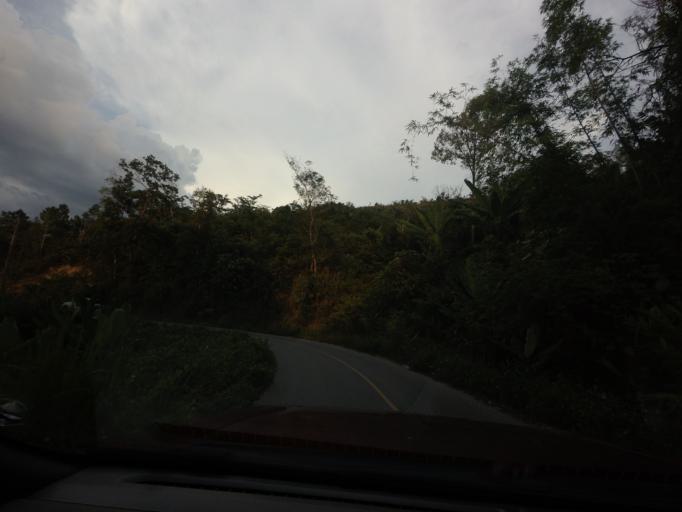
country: TH
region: Yala
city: Than To
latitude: 6.0079
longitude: 101.2255
